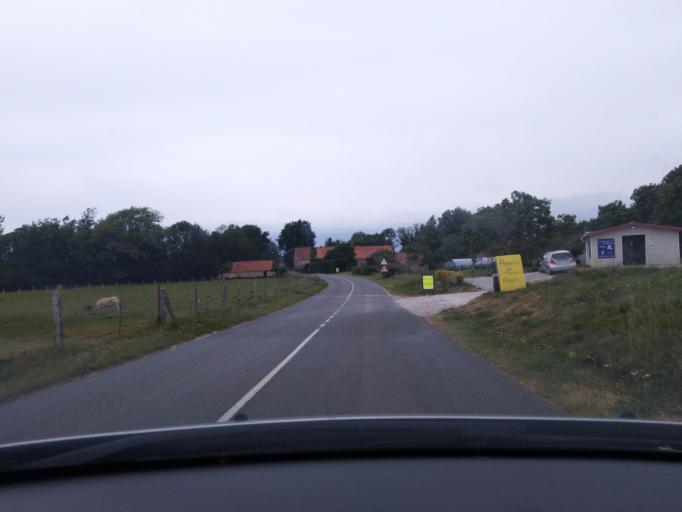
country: FR
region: Nord-Pas-de-Calais
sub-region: Departement du Pas-de-Calais
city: Marquise
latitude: 50.8327
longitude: 1.6879
